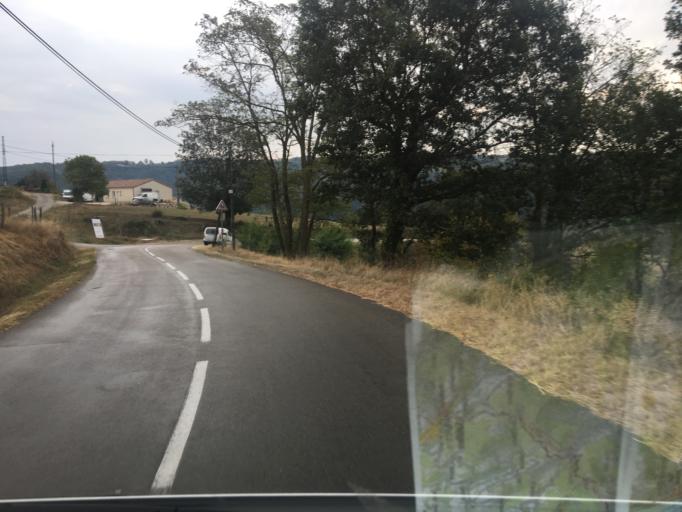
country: FR
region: Rhone-Alpes
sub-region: Departement de l'Ardeche
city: Saint-Felicien
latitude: 45.0550
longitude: 4.7062
